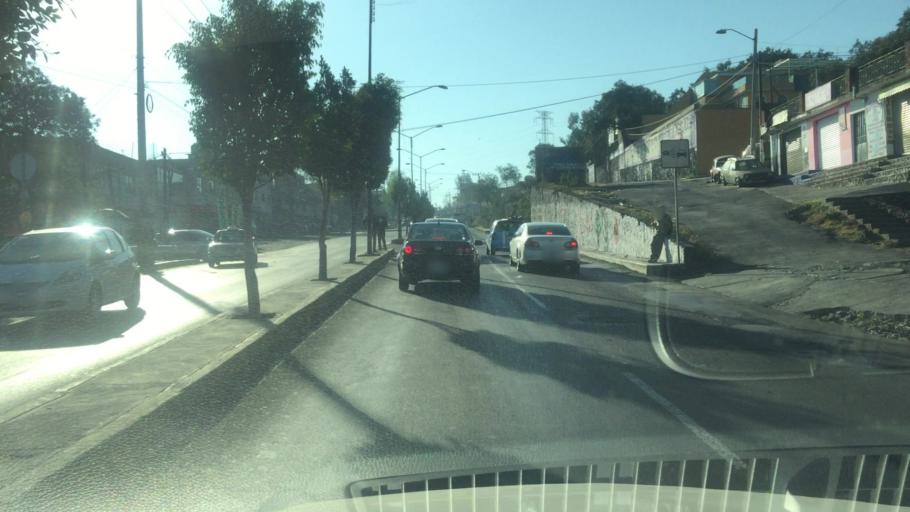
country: MX
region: Mexico City
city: Tlalpan
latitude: 19.2770
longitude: -99.2092
